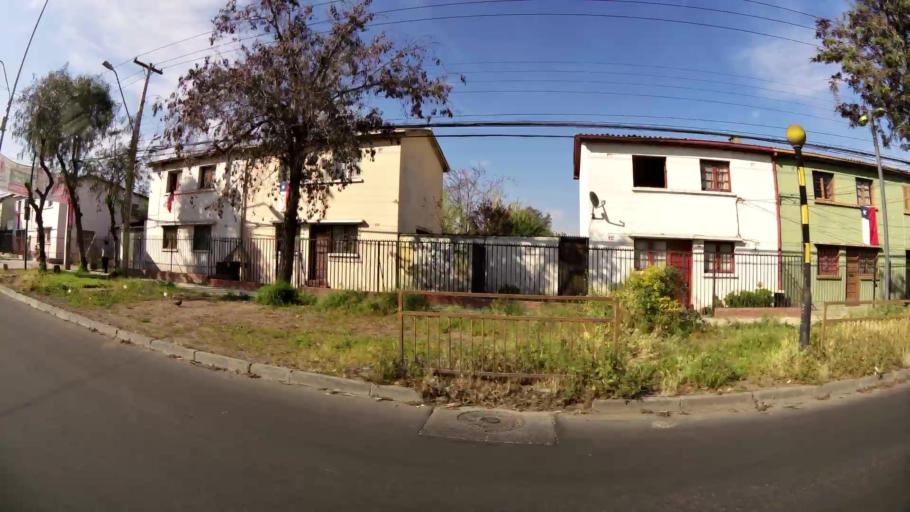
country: CL
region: Santiago Metropolitan
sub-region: Provincia de Santiago
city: Santiago
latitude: -33.4150
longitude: -70.6731
